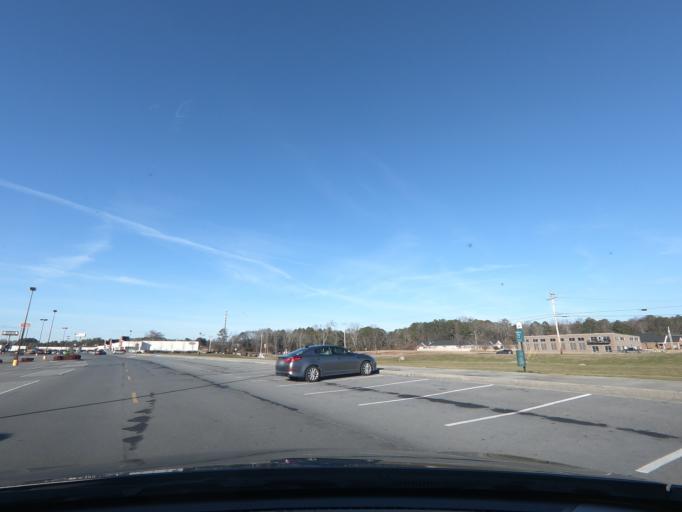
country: US
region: Georgia
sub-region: Gordon County
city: Calhoun
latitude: 34.4591
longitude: -84.9175
